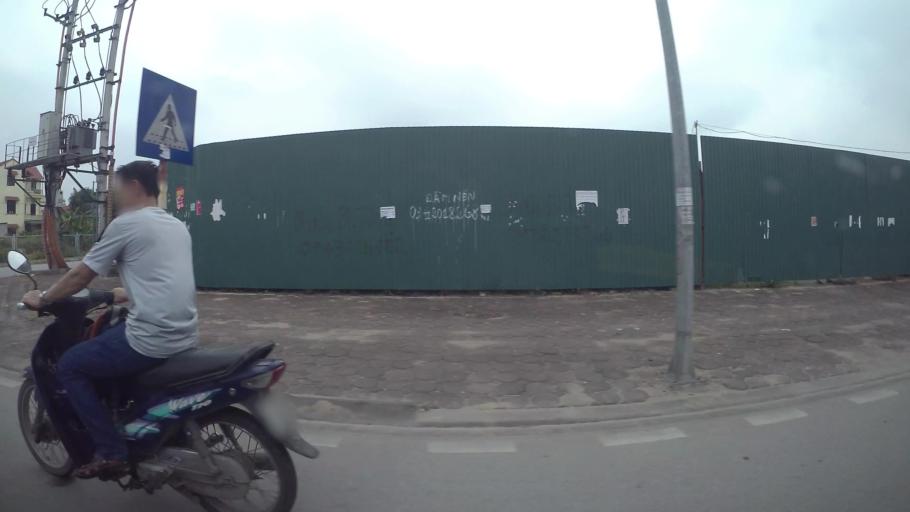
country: VN
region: Ha Noi
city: Trau Quy
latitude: 21.0527
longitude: 105.9205
